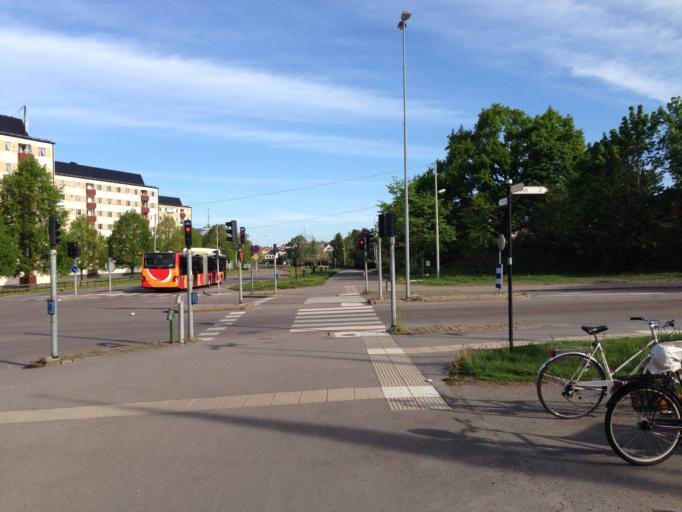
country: SE
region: OEstergoetland
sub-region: Linkopings Kommun
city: Linkoping
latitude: 58.3933
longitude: 15.6459
